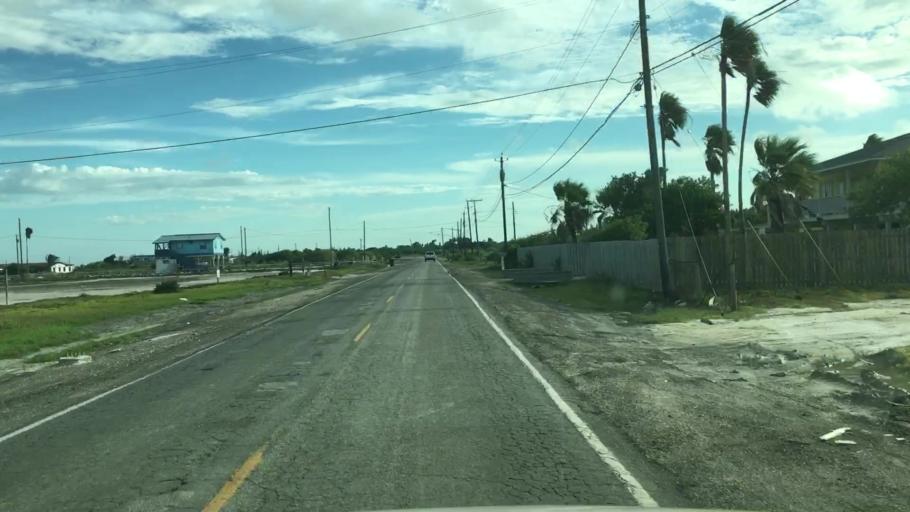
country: US
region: Texas
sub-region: Nueces County
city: Corpus Christi
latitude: 27.6419
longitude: -97.2857
